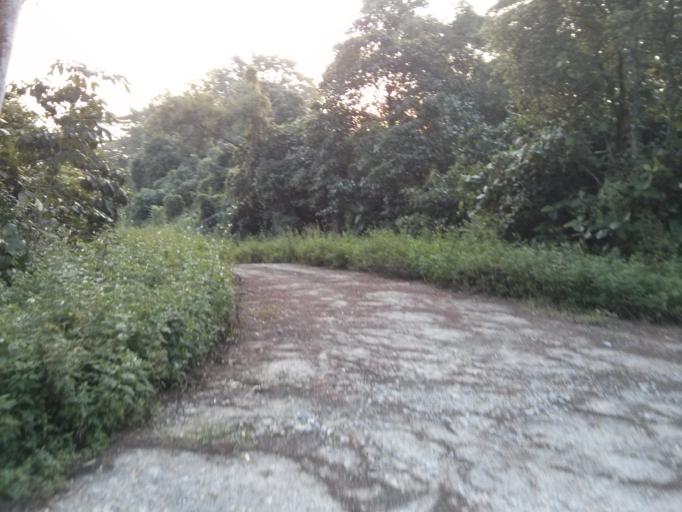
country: MY
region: Johor
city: Johor Bahru
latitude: 1.3756
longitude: 103.7332
